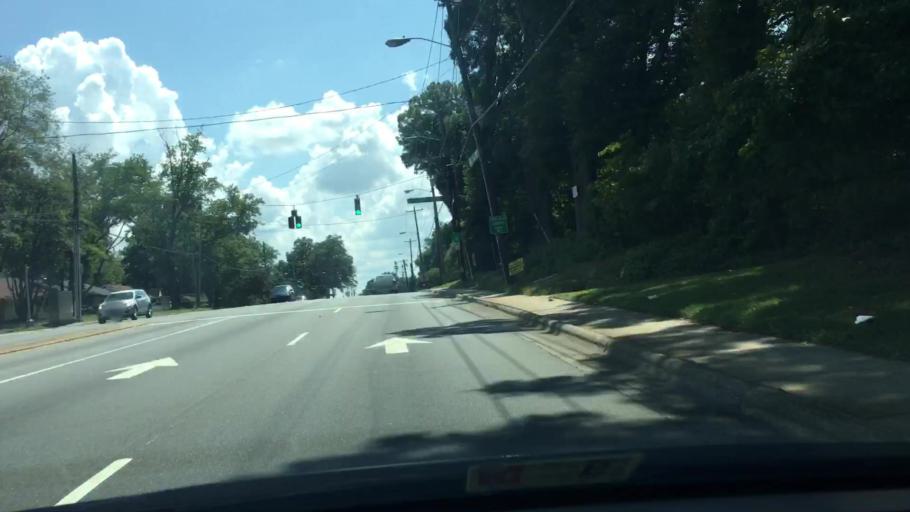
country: US
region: North Carolina
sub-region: Mecklenburg County
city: Charlotte
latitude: 35.2713
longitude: -80.7941
